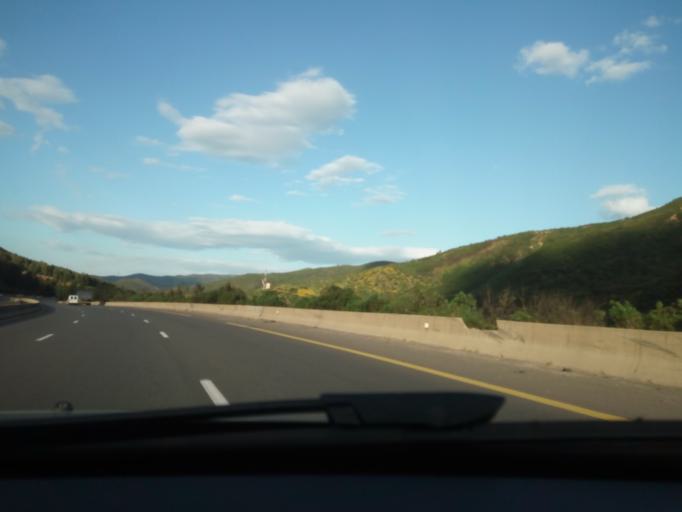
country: DZ
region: Tipaza
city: El Affroun
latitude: 36.3915
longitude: 2.5224
